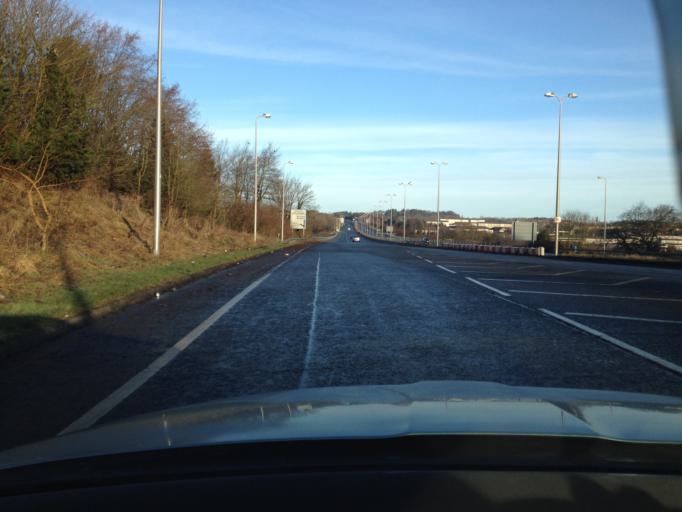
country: GB
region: Scotland
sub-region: West Lothian
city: Mid Calder
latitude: 55.8870
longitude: -3.5006
